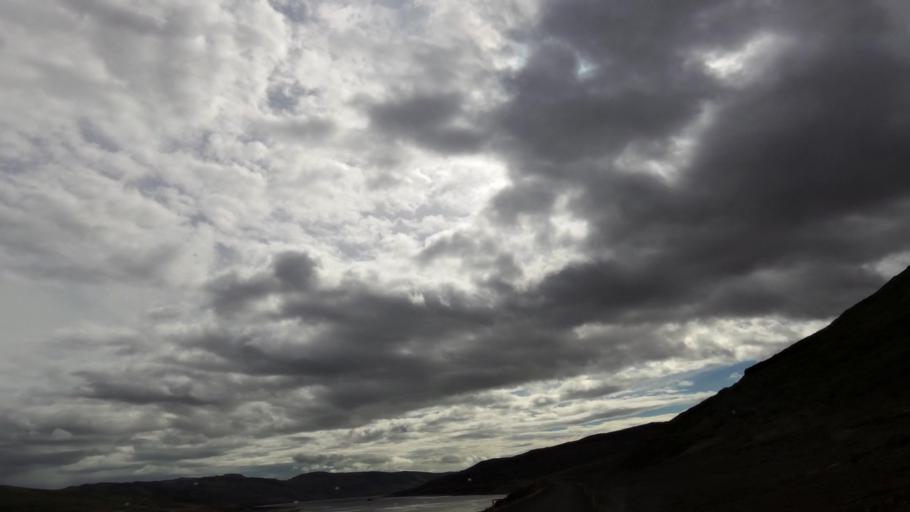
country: IS
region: West
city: Stykkisholmur
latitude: 65.5943
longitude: -22.1265
